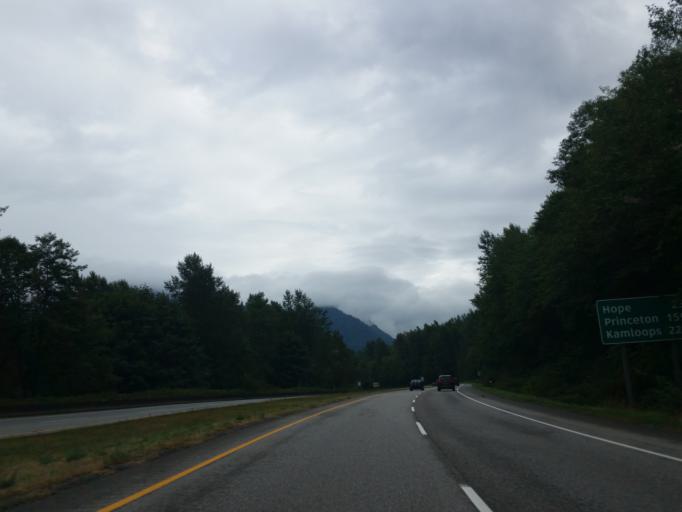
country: CA
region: British Columbia
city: Agassiz
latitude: 49.2811
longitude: -121.6711
